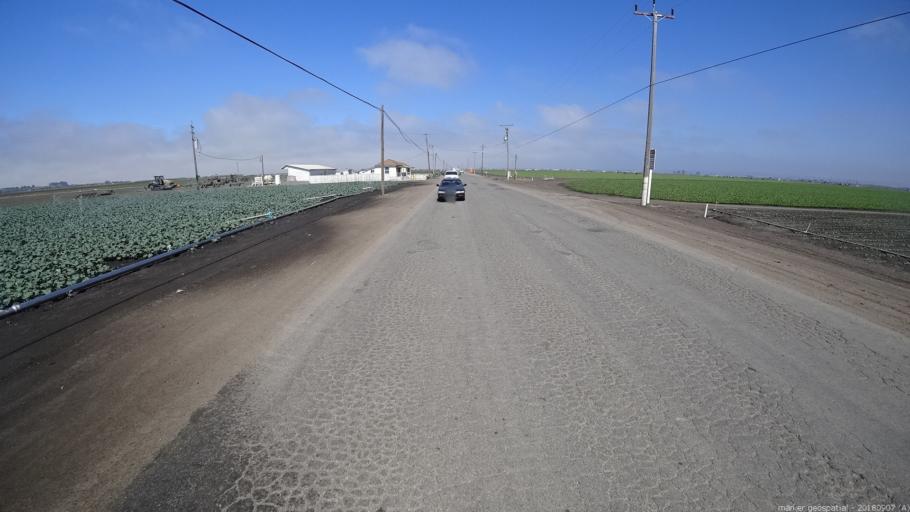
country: US
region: California
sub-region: Monterey County
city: Castroville
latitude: 36.7110
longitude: -121.7390
